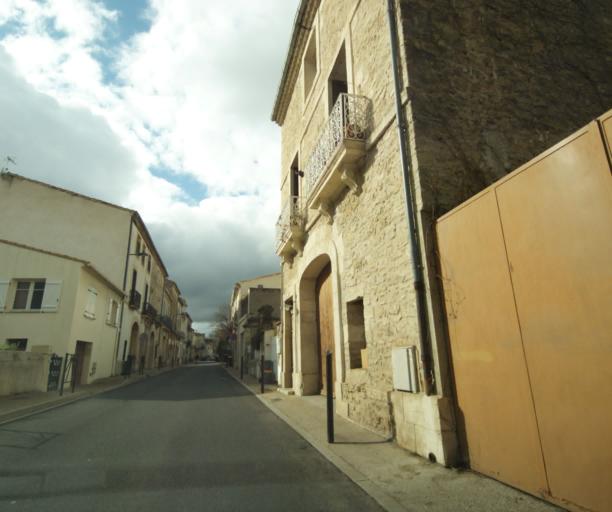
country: FR
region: Languedoc-Roussillon
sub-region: Departement de l'Herault
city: Pignan
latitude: 43.5813
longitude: 3.7655
